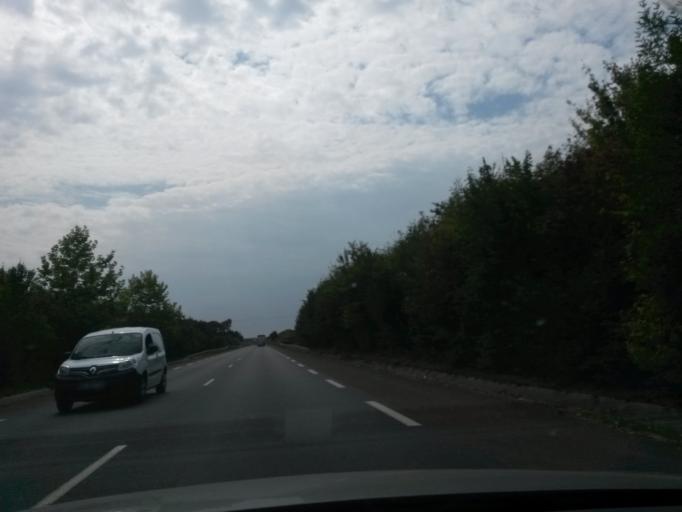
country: FR
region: Poitou-Charentes
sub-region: Departement de la Charente-Maritime
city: Saint-Xandre
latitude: 46.1902
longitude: -1.0942
